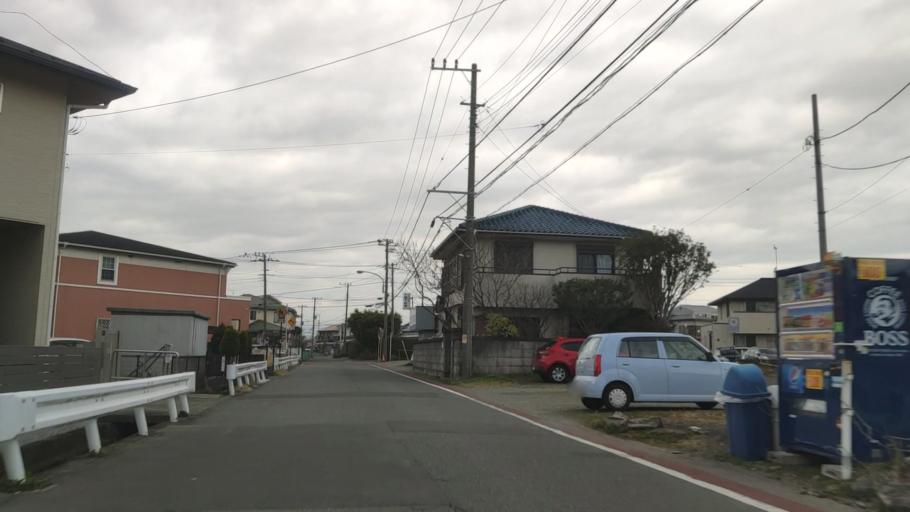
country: JP
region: Kanagawa
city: Odawara
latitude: 35.2751
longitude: 139.1881
